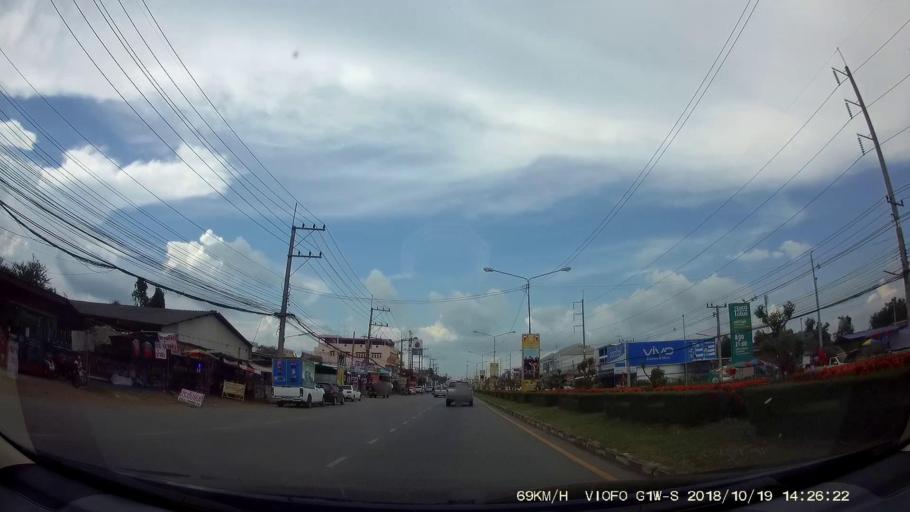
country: TH
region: Chaiyaphum
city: Kaeng Khro
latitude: 16.1056
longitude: 102.2600
